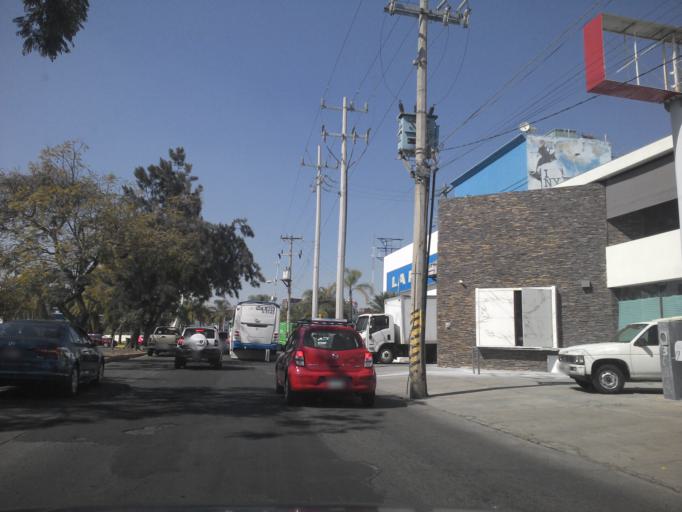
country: MX
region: Jalisco
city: Guadalajara
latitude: 20.6787
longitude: -103.3927
